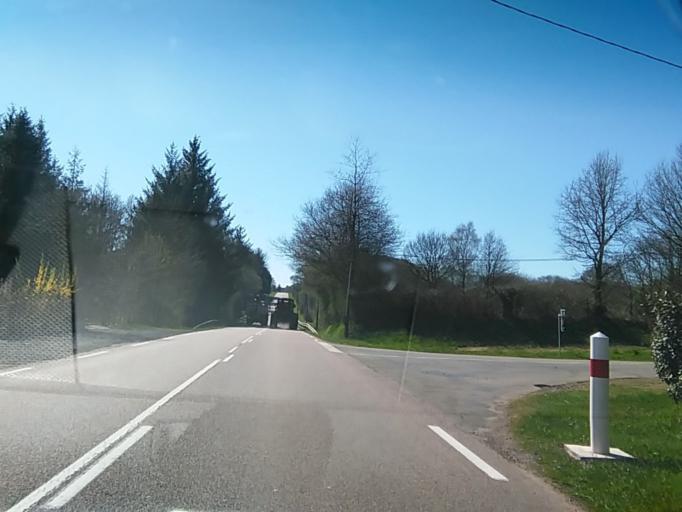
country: FR
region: Lower Normandy
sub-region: Departement de l'Orne
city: Magny-le-Desert
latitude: 48.5832
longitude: -0.2171
